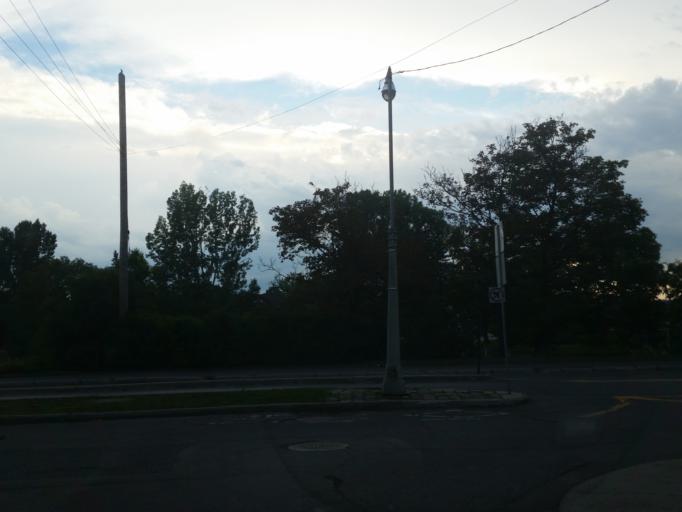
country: CA
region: Ontario
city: Ottawa
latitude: 45.4112
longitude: -75.6822
